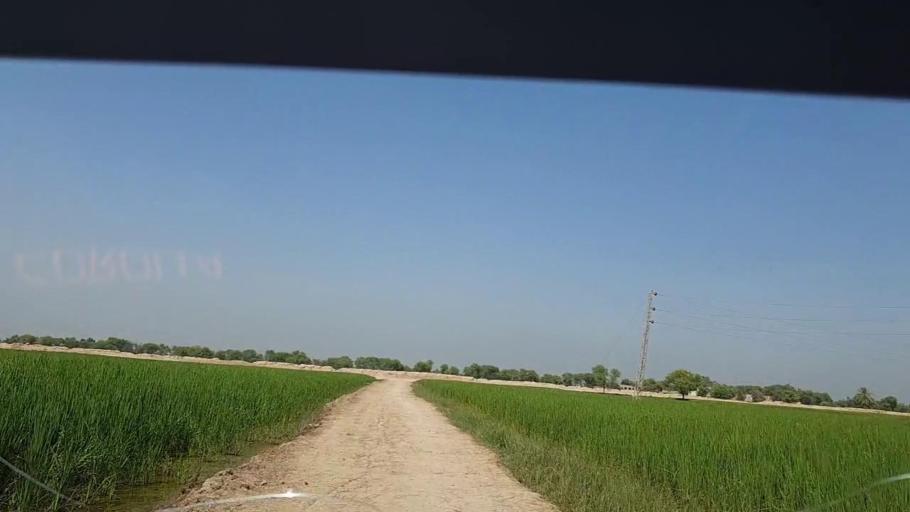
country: PK
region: Sindh
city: Tangwani
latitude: 28.2867
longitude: 69.0398
